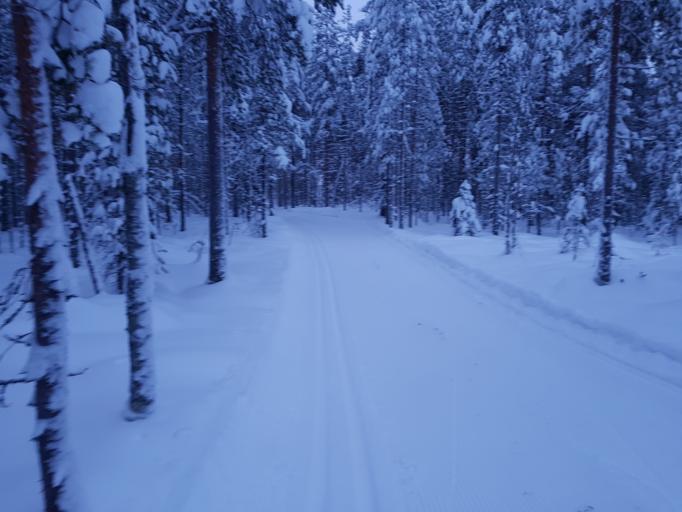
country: FI
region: Kainuu
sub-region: Kehys-Kainuu
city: Kuhmo
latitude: 64.0877
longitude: 29.5137
